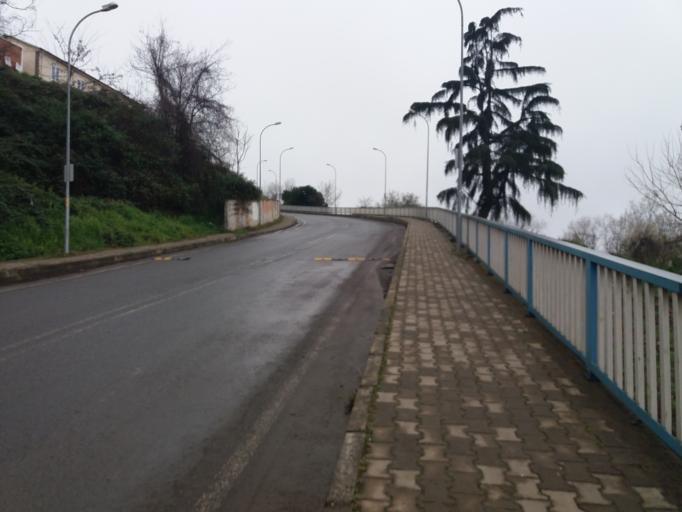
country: TR
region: Trabzon
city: Trabzon
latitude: 40.9921
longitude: 39.7729
